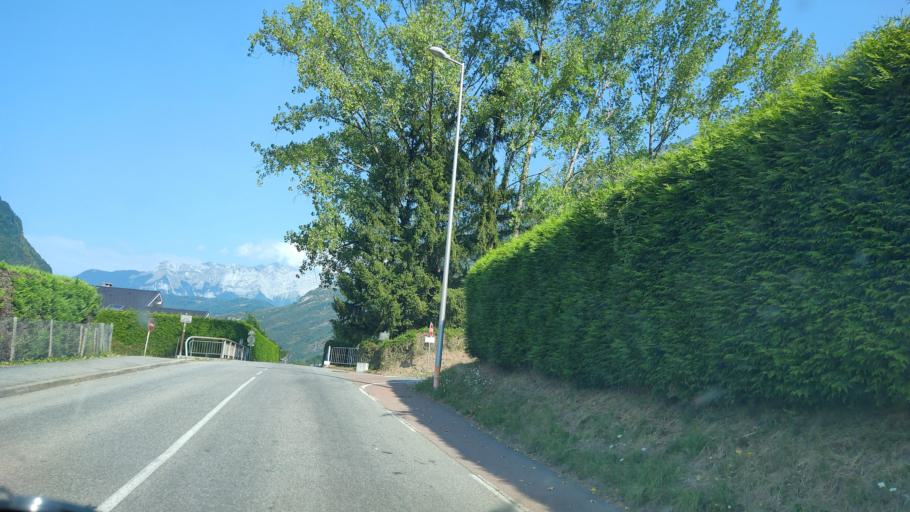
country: FR
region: Rhone-Alpes
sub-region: Departement de la Savoie
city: Ugine
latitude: 45.7575
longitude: 6.4085
